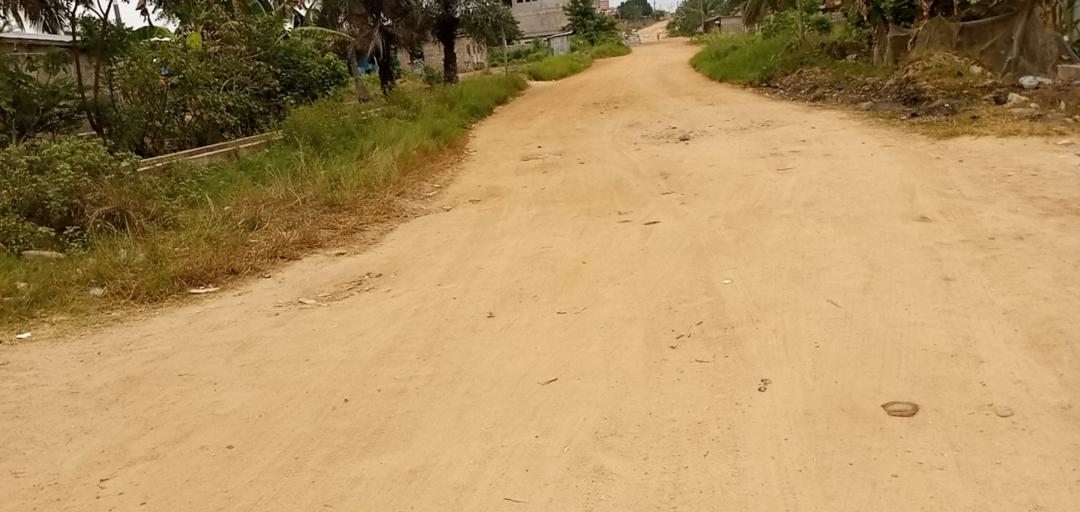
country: GH
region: Central
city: Winneba
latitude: 5.3533
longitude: -0.6253
